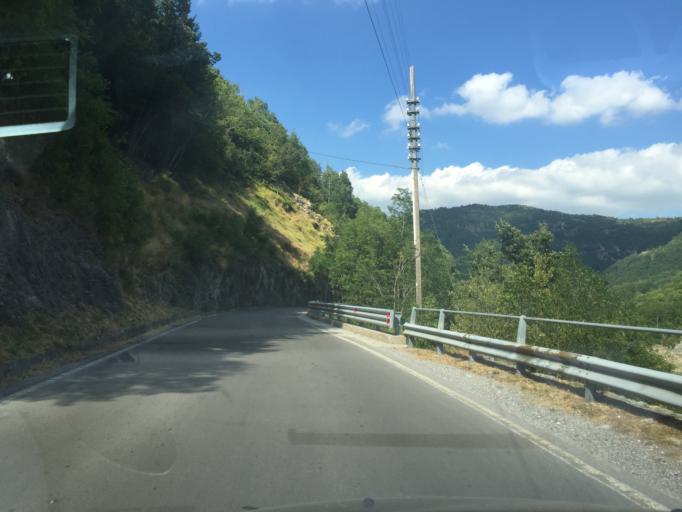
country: IT
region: Tuscany
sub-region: Provincia di Lucca
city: Fontana delle Monache
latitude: 44.1165
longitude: 10.2955
